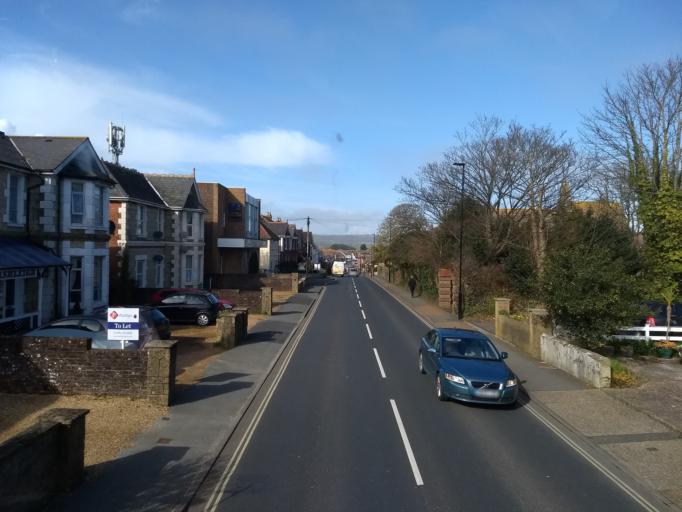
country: GB
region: England
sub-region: Isle of Wight
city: Sandown
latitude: 50.6457
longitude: -1.1686
